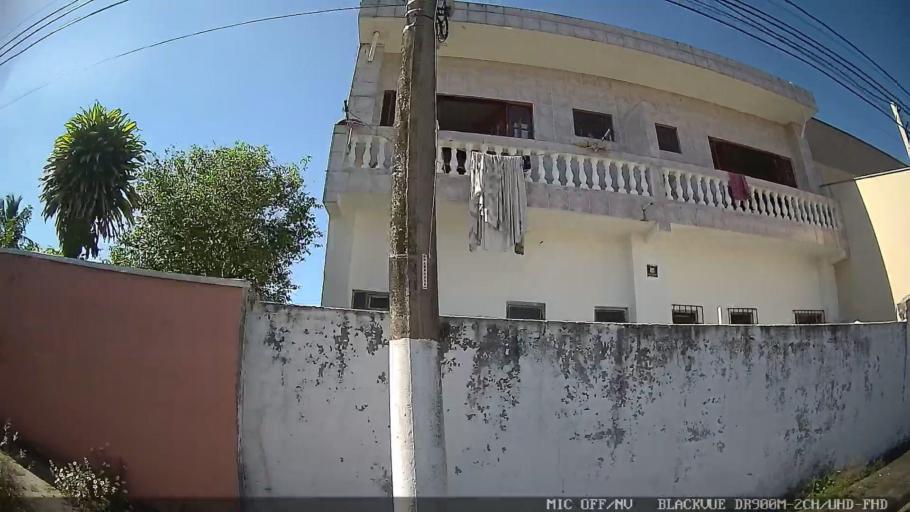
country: BR
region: Sao Paulo
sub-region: Peruibe
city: Peruibe
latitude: -24.2758
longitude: -46.9437
